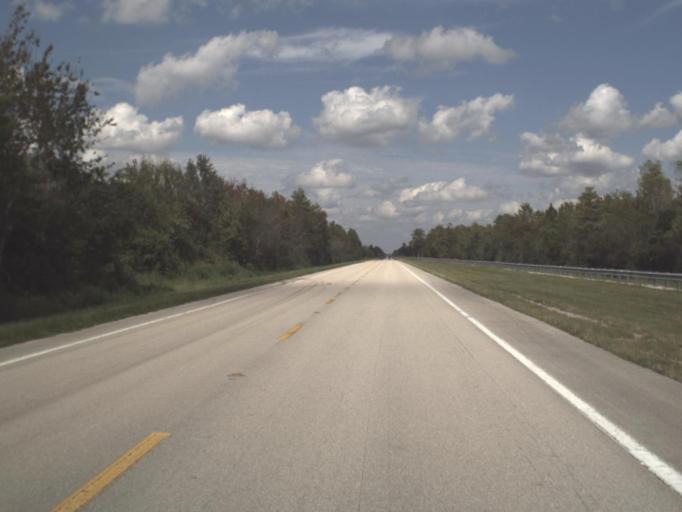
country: US
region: Florida
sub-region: Collier County
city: Orangetree
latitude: 26.0595
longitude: -81.3445
